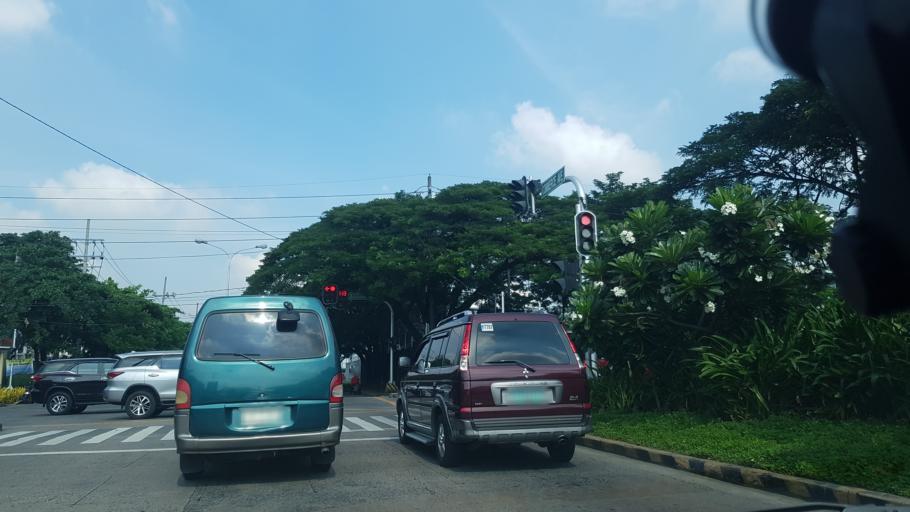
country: PH
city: Sambayanihan People's Village
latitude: 14.4226
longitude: 121.0273
